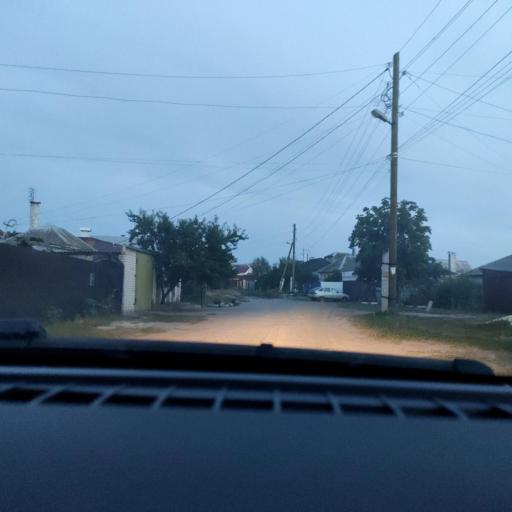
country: RU
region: Voronezj
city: Maslovka
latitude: 51.5575
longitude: 39.2359
